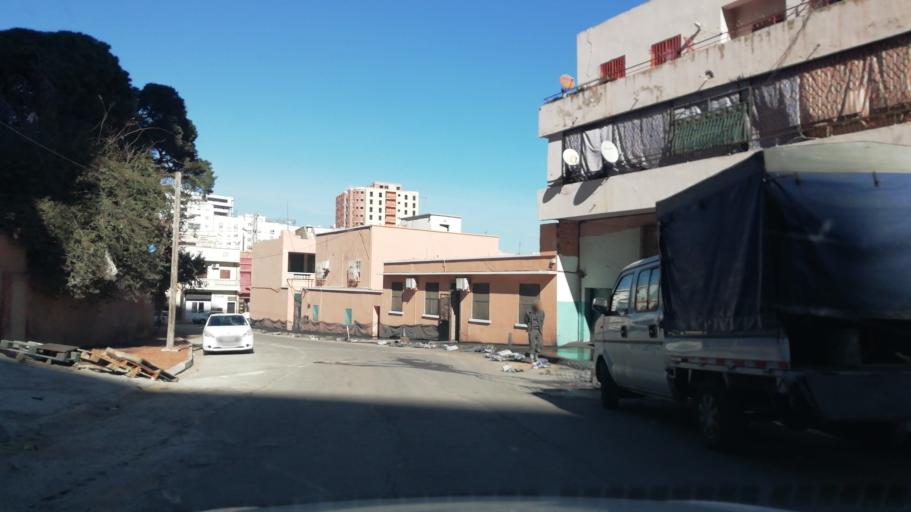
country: DZ
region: Oran
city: Oran
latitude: 35.7019
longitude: -0.6225
